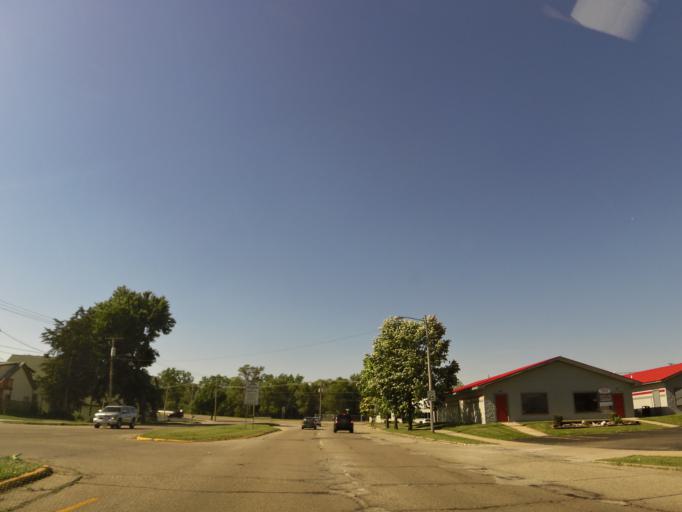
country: US
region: Wisconsin
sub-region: Rock County
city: Beloit
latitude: 42.4962
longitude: -89.0200
